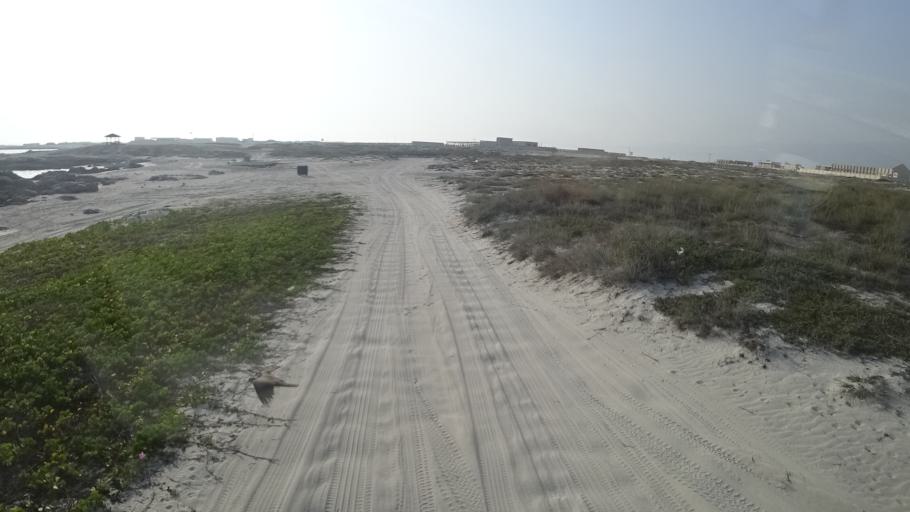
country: OM
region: Zufar
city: Salalah
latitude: 16.9690
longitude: 54.7052
